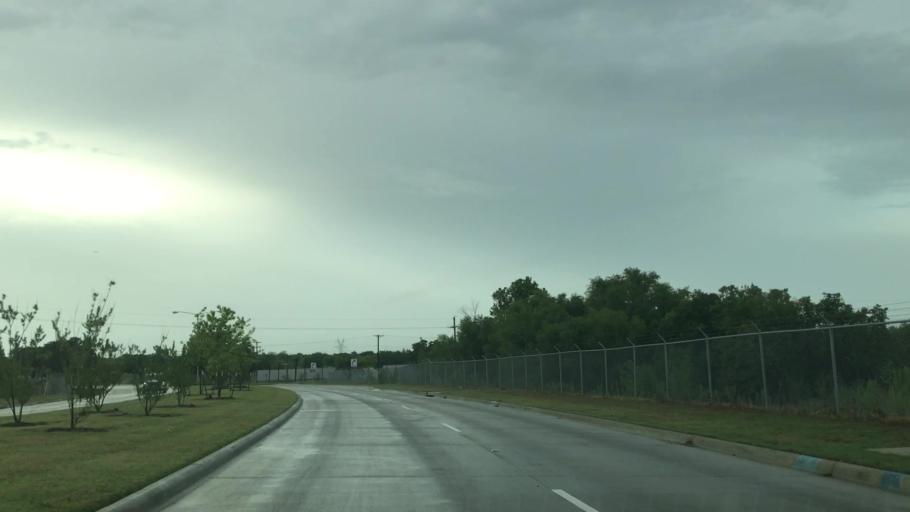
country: US
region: Texas
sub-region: Denton County
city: Lewisville
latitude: 33.0555
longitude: -96.9828
